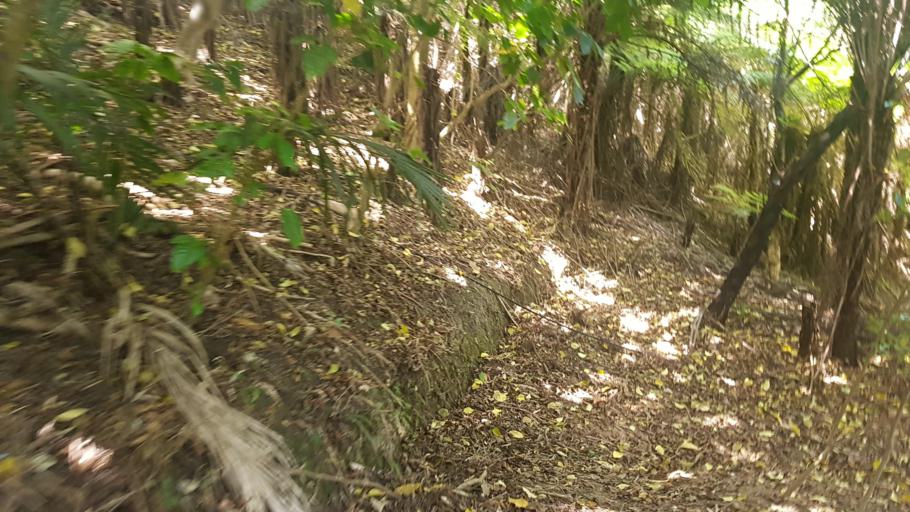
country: NZ
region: Auckland
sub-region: Auckland
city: Pakuranga
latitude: -36.8436
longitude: 175.1460
